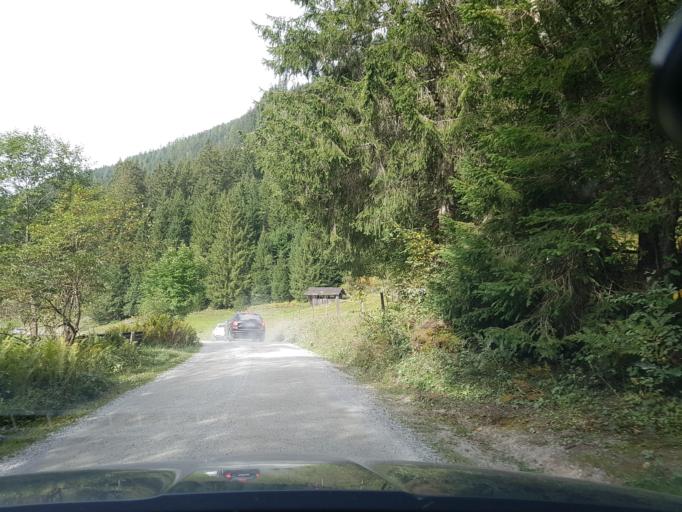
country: AT
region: Salzburg
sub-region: Politischer Bezirk Sankt Johann im Pongau
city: Forstau
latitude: 47.3497
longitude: 13.5727
